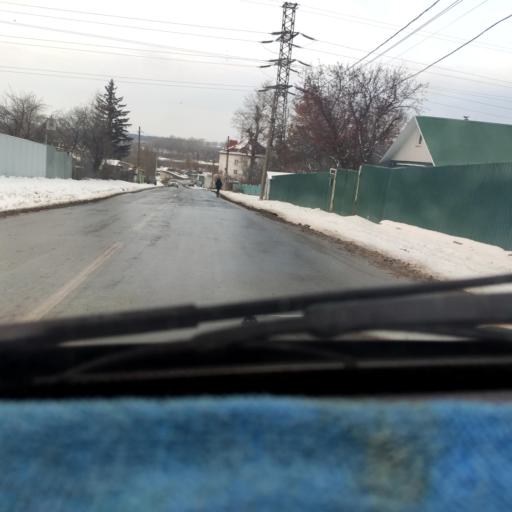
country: RU
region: Bashkortostan
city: Ufa
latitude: 54.8307
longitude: 56.0615
